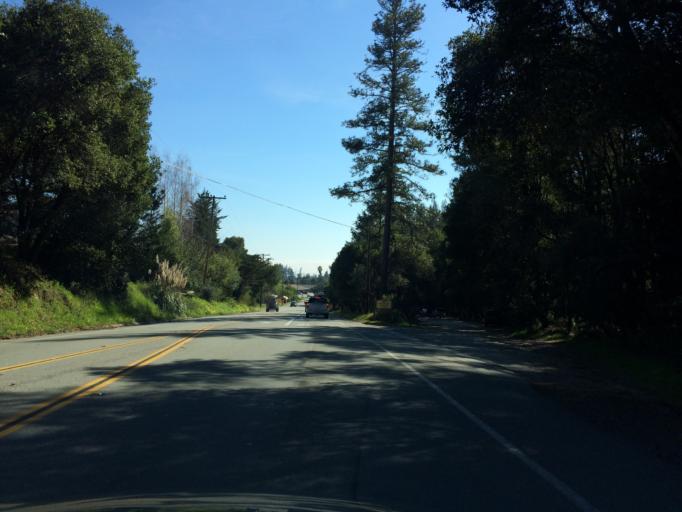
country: US
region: California
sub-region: Santa Cruz County
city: Pasatiempo
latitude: 37.0172
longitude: -122.0353
